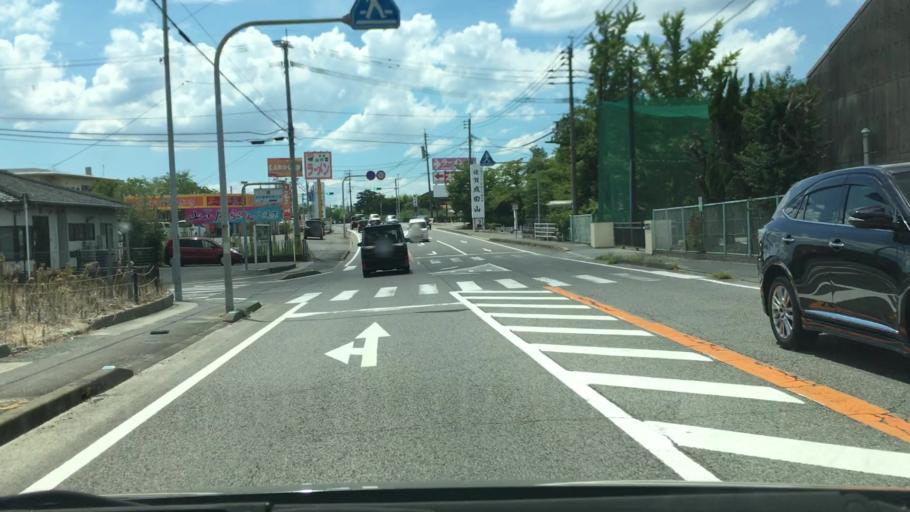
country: JP
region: Saga Prefecture
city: Kanzakimachi-kanzaki
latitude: 33.3366
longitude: 130.4201
